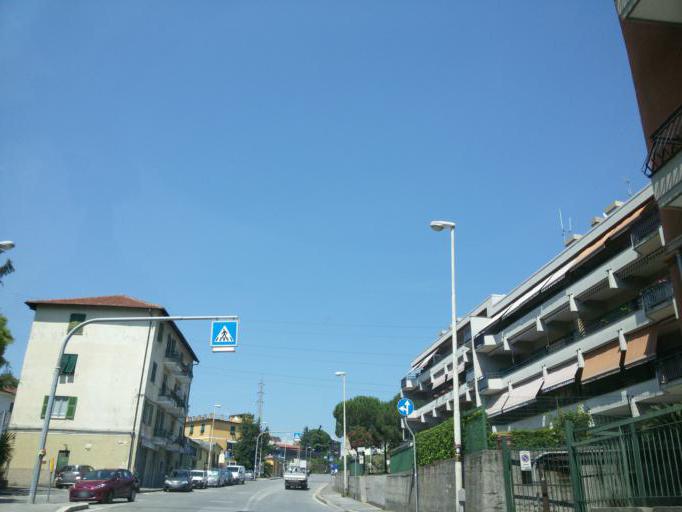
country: IT
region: Liguria
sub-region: Provincia di Genova
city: San Teodoro
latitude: 44.4357
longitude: 8.8723
